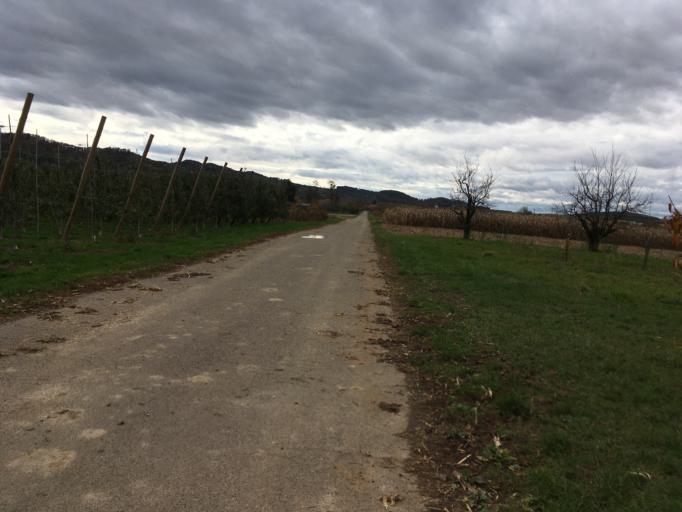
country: DE
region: Baden-Wuerttemberg
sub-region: Freiburg Region
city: Wyhl
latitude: 48.1446
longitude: 7.6690
